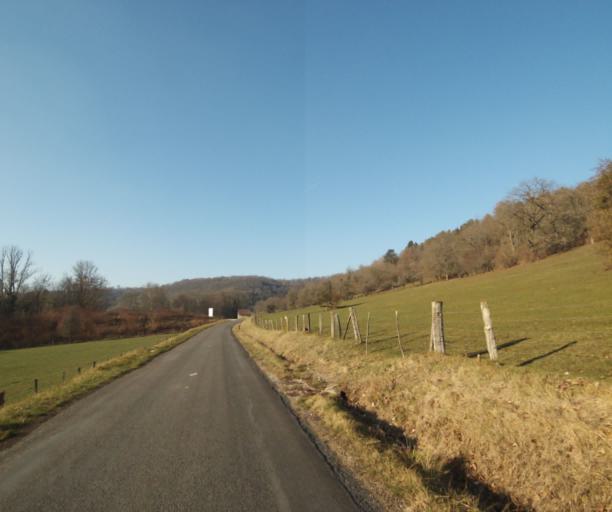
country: FR
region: Champagne-Ardenne
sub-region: Departement de la Haute-Marne
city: Chevillon
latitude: 48.5020
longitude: 5.1792
